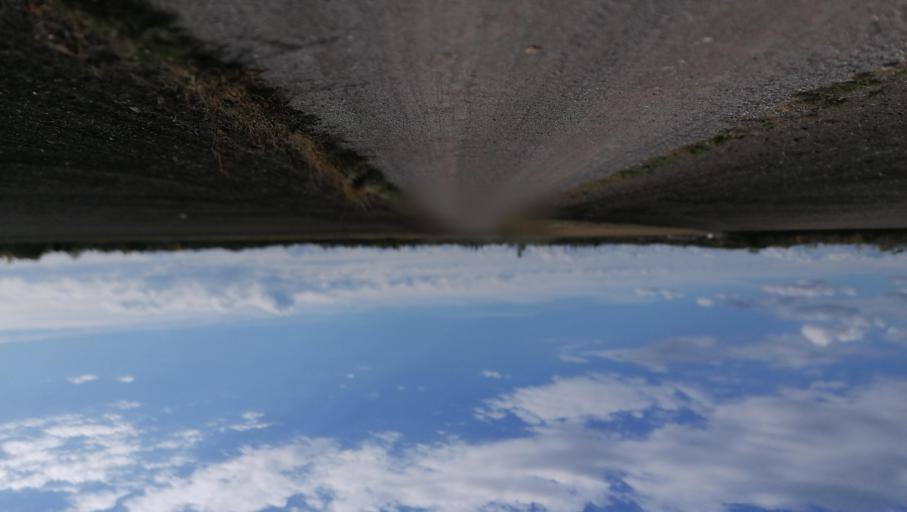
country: AT
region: Lower Austria
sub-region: Politischer Bezirk Baden
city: Teesdorf
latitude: 47.9695
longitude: 16.2876
